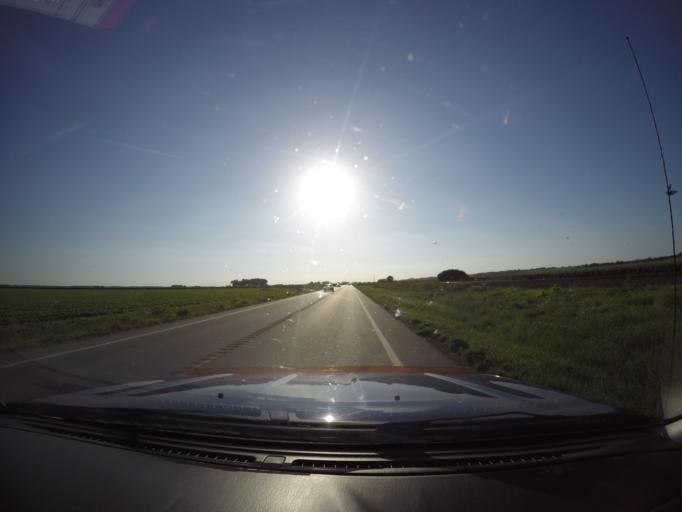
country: US
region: Kansas
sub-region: Shawnee County
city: Silver Lake
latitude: 39.1087
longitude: -95.8733
